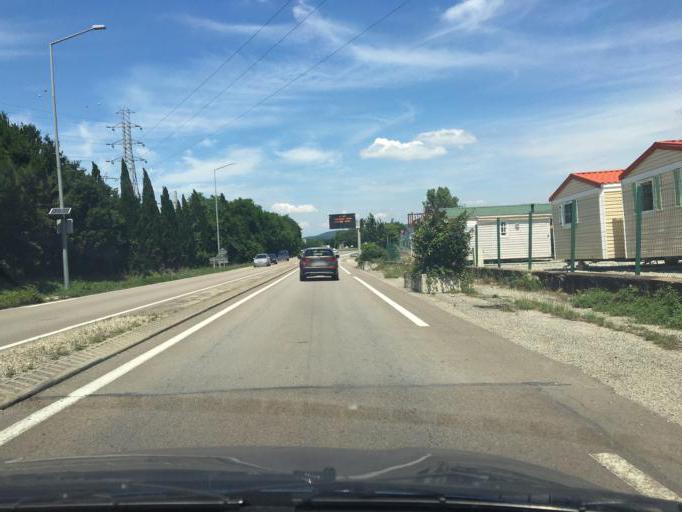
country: FR
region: Rhone-Alpes
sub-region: Departement de l'Ardeche
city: Cruas
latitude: 44.6654
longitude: 4.7918
